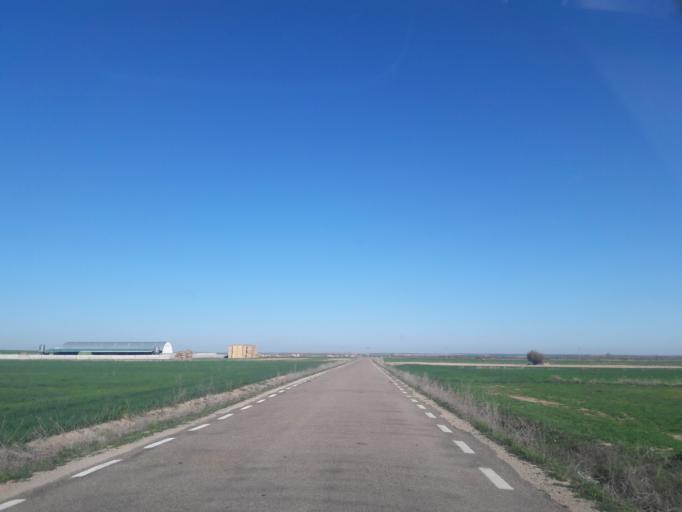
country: ES
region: Castille and Leon
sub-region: Provincia de Salamanca
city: Coca de Alba
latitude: 40.8666
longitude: -5.3727
